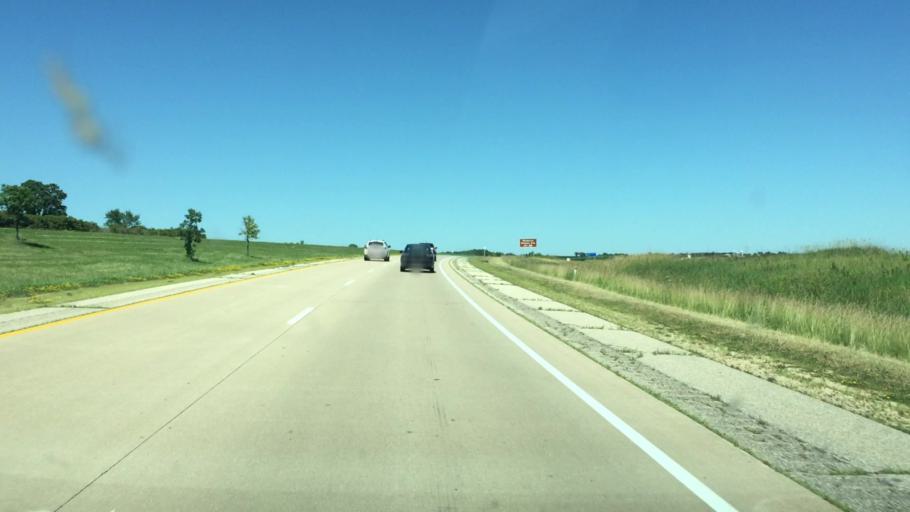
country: US
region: Wisconsin
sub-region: Iowa County
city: Mineral Point
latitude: 42.8783
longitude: -90.1878
